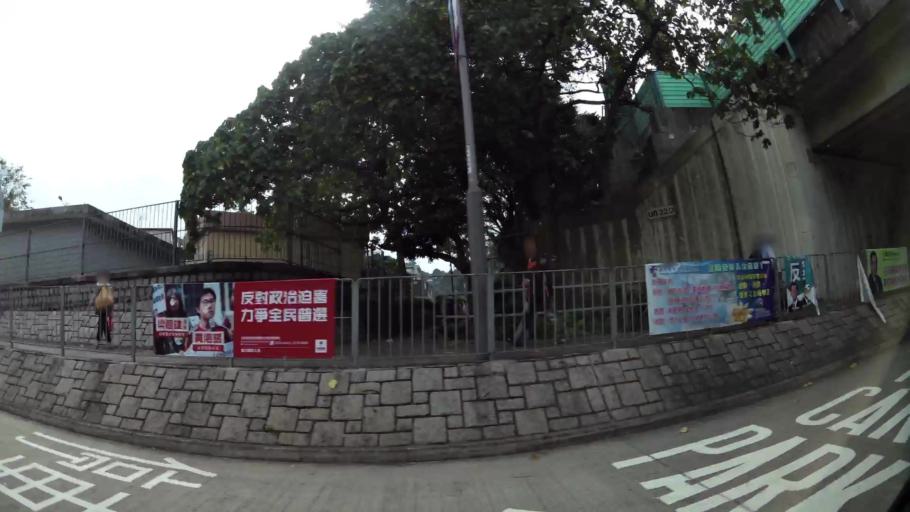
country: HK
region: Tai Po
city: Tai Po
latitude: 22.4453
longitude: 114.1667
